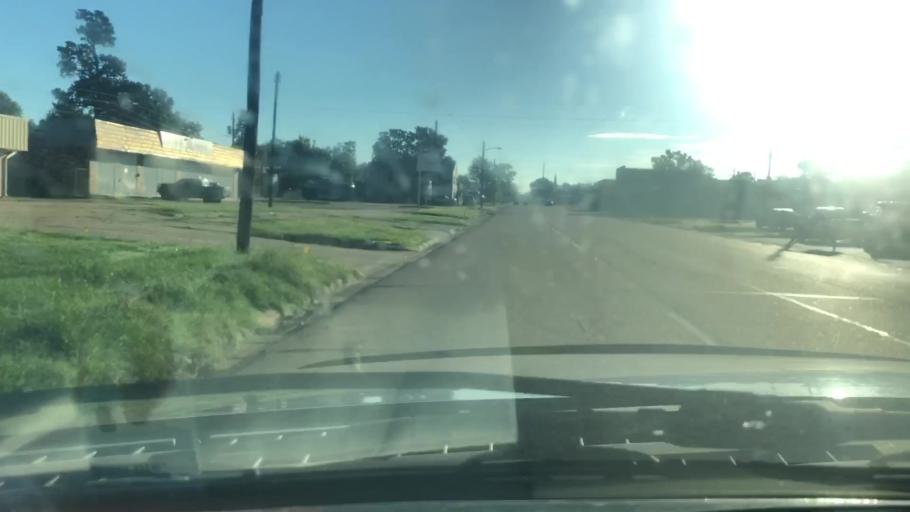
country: US
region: Texas
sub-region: Bowie County
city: Texarkana
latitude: 33.4232
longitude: -94.0651
